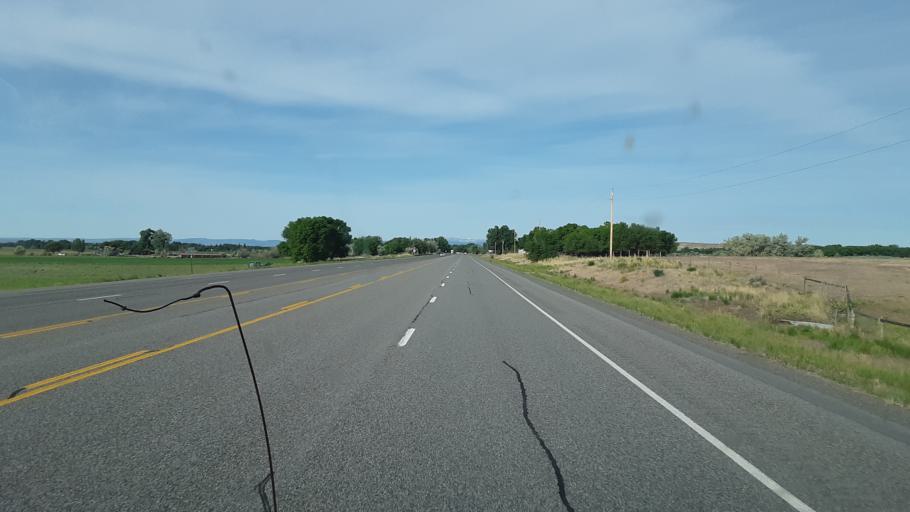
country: US
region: Wyoming
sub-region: Fremont County
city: Riverton
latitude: 43.0915
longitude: -108.3671
